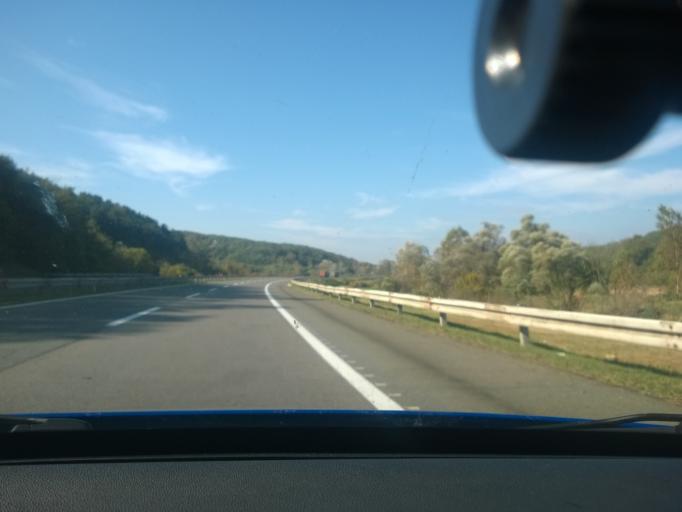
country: RS
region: Central Serbia
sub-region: Rasinski Okrug
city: Cicevac
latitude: 43.7401
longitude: 21.4915
